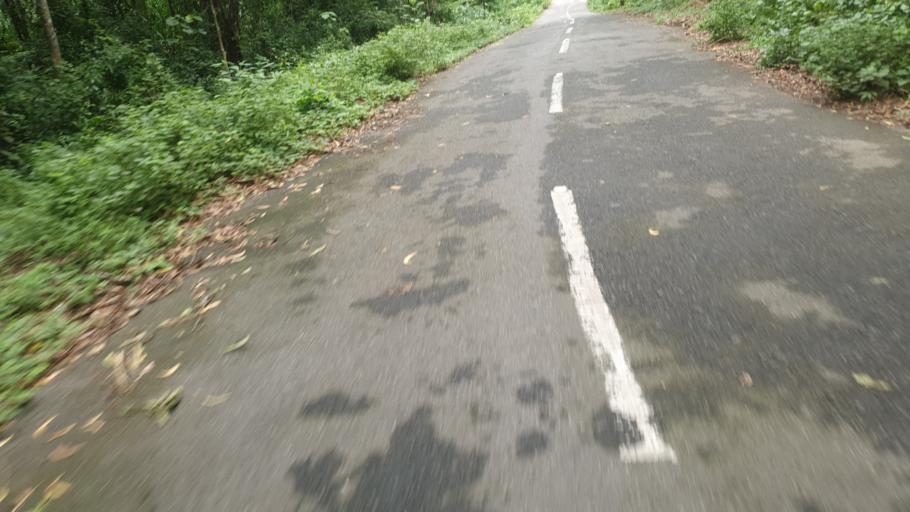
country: IN
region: Kerala
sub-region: Thiruvananthapuram
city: Nedumangad
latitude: 8.6455
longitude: 77.1095
